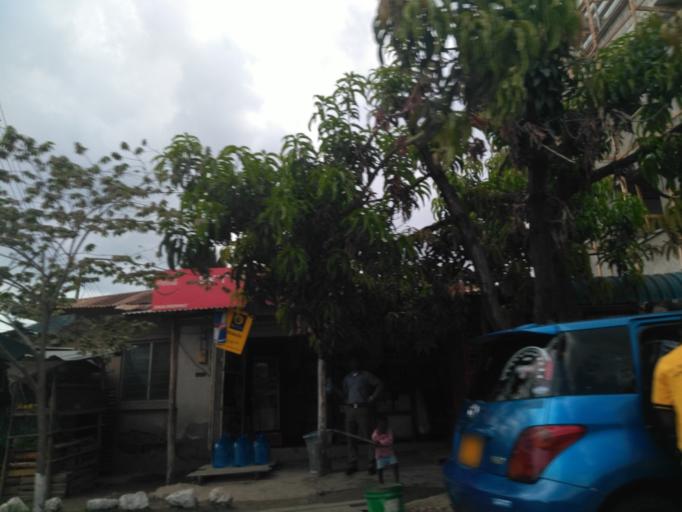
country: TZ
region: Dar es Salaam
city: Magomeni
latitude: -6.7535
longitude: 39.2430
